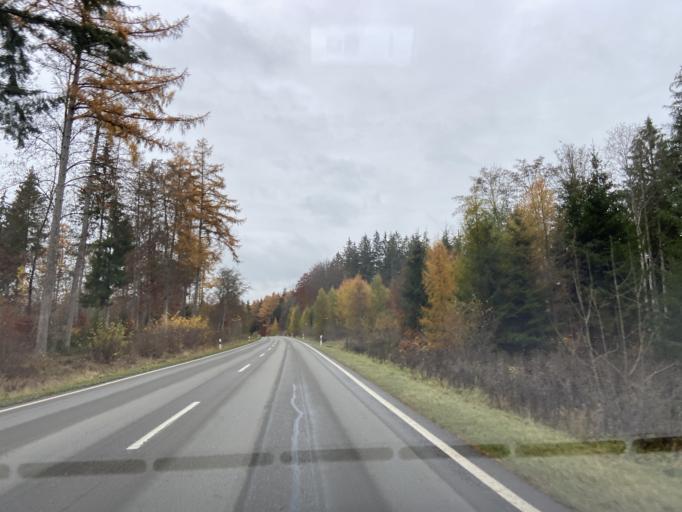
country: DE
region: Baden-Wuerttemberg
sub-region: Tuebingen Region
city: Messkirch
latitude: 47.9749
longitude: 9.1456
